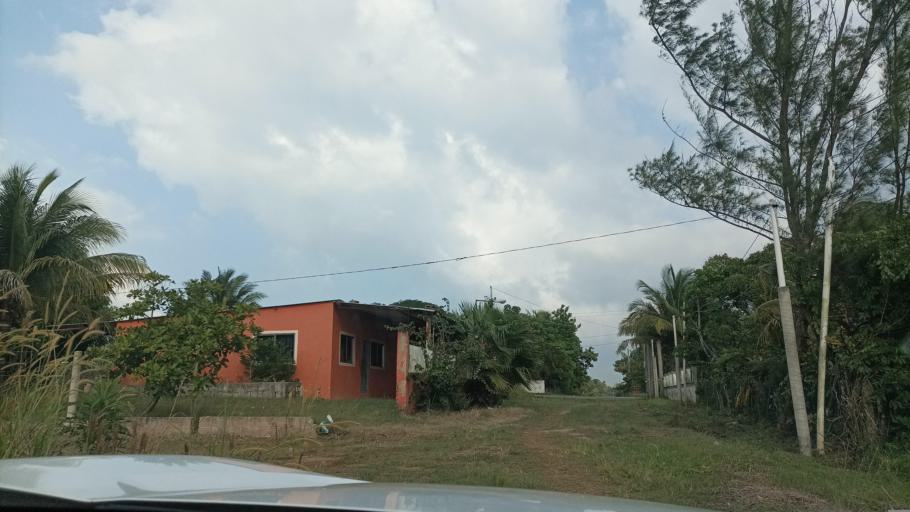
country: MX
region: Veracruz
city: Allende
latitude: 18.1572
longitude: -94.3256
